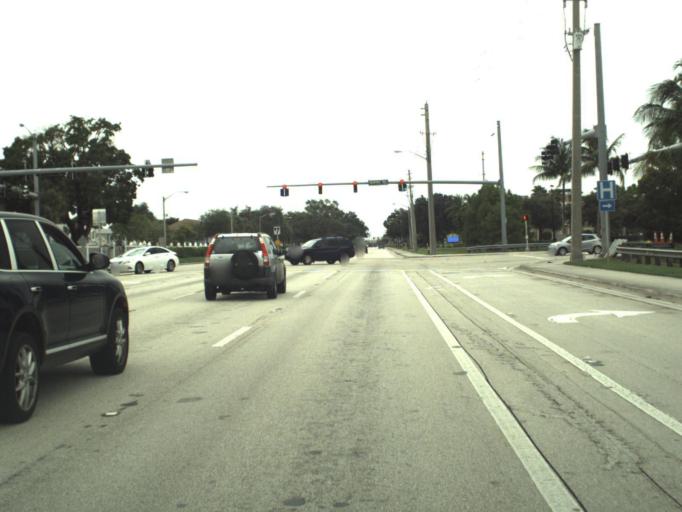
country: US
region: Florida
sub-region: Palm Beach County
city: North Palm Beach
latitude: 26.8302
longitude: -80.1054
